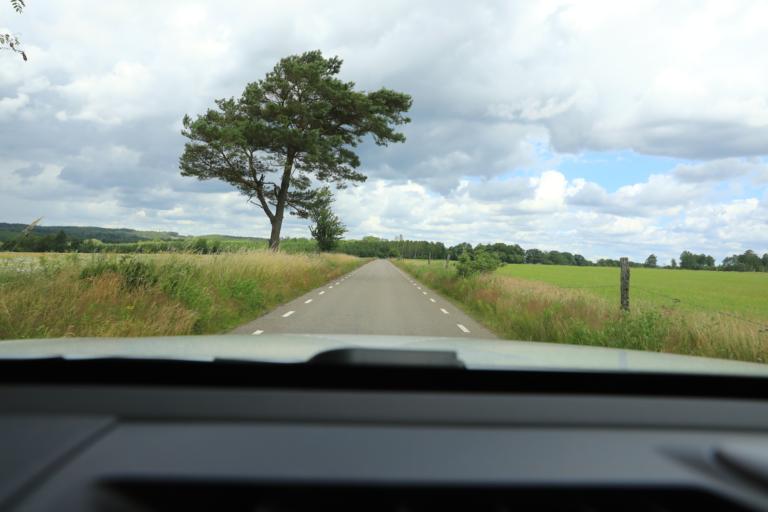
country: SE
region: Halland
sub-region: Varbergs Kommun
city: Tvaaker
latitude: 57.0476
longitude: 12.4649
